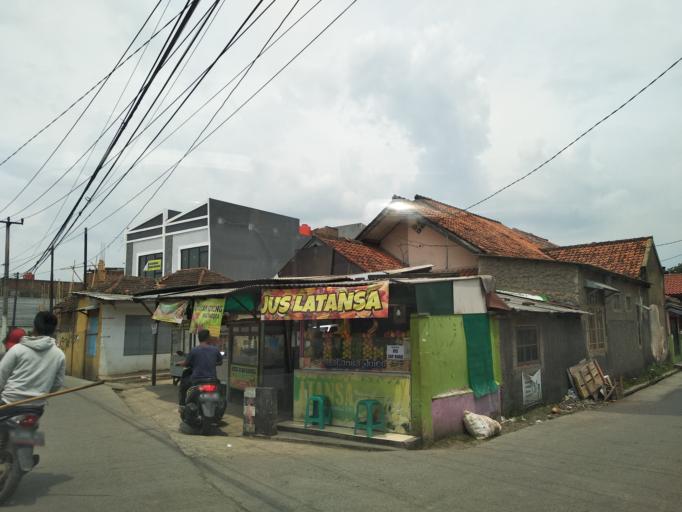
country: ID
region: West Java
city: Pameungpeuk
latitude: -6.9721
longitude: 107.6481
